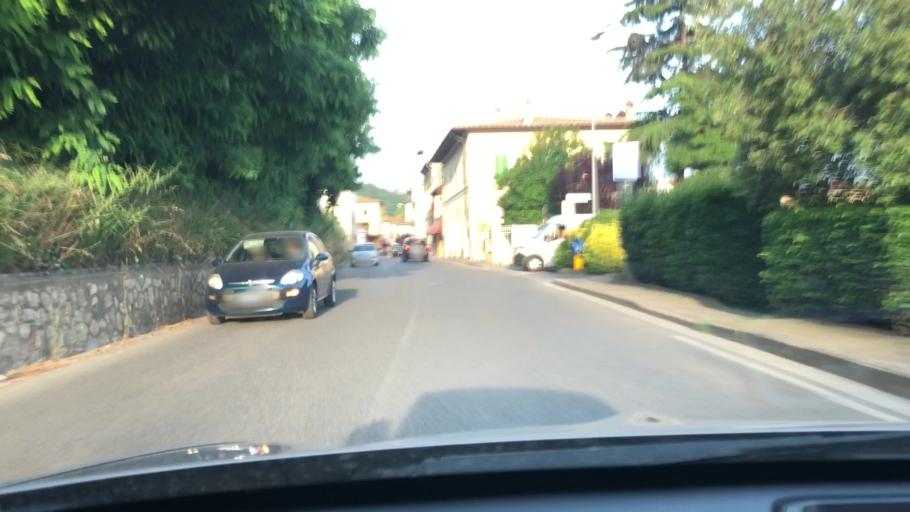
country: IT
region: Tuscany
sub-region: Province of Pisa
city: Forcoli
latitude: 43.6051
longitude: 10.7013
